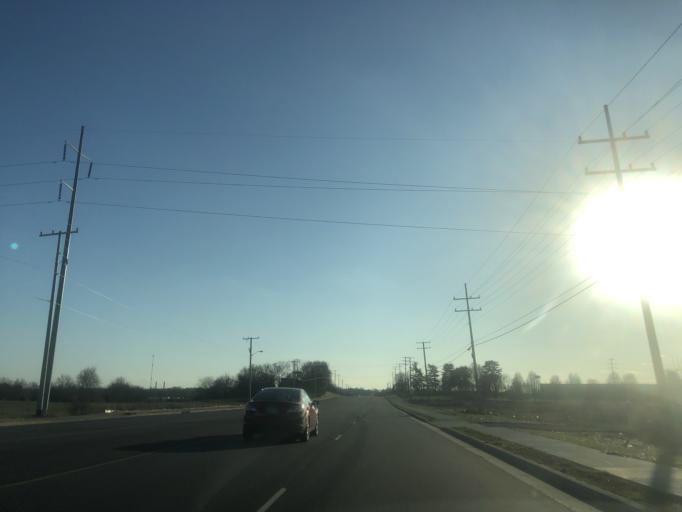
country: US
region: Tennessee
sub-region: Sumner County
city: Portland
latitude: 36.6322
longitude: -86.5647
